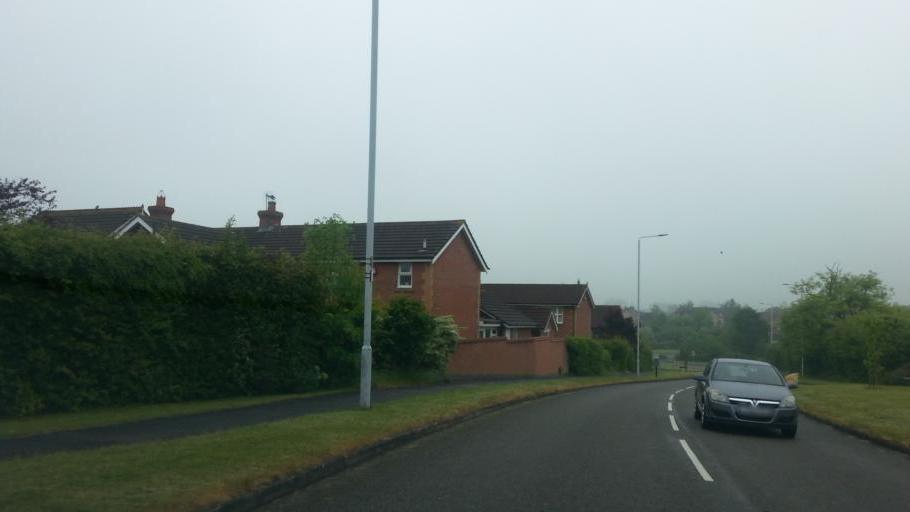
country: GB
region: England
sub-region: Leicestershire
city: Great Glen
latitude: 52.5919
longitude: -1.0551
